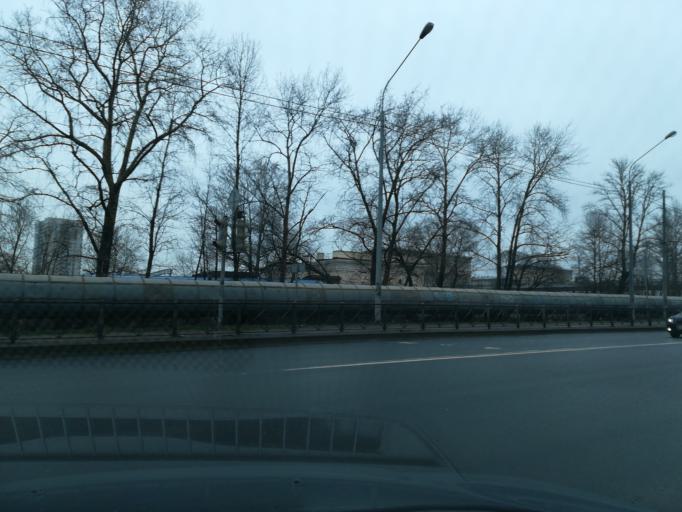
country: RU
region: St.-Petersburg
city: Avtovo
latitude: 59.8630
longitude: 30.2549
